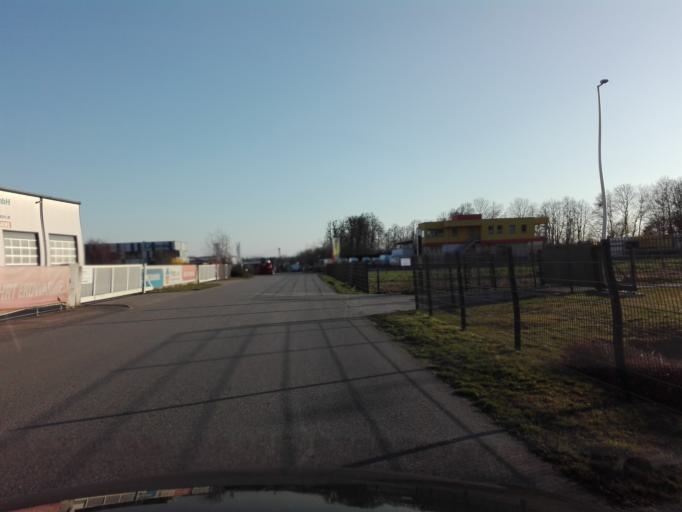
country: AT
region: Upper Austria
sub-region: Politischer Bezirk Perg
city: Perg
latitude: 48.2273
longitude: 14.6990
